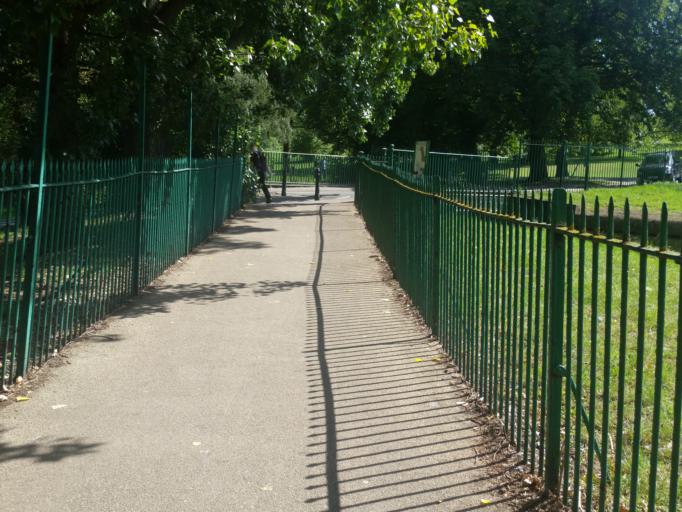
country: GB
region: England
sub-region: Greater London
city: Harringay
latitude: 51.5745
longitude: -0.1010
